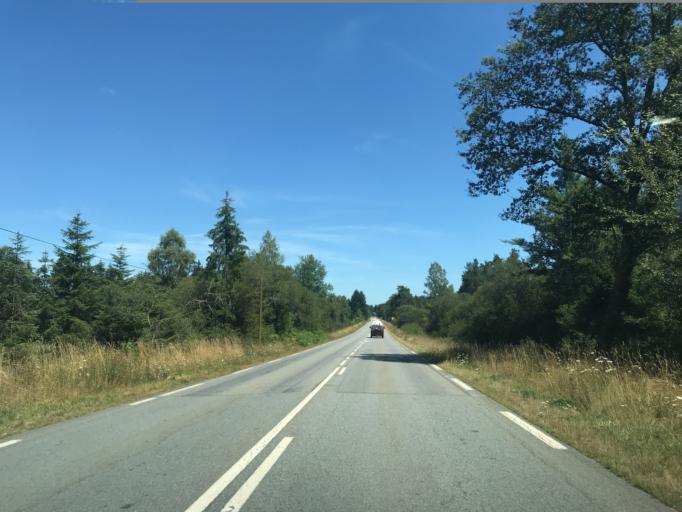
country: FR
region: Limousin
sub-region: Departement de la Correze
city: Meymac
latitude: 45.4956
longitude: 2.2178
